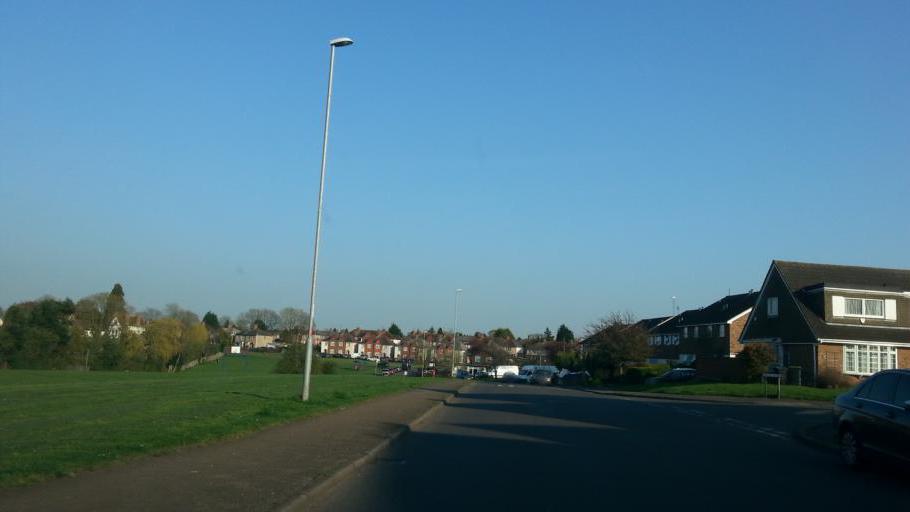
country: GB
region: England
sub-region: Northamptonshire
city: Rushden
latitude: 52.2916
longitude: -0.6197
